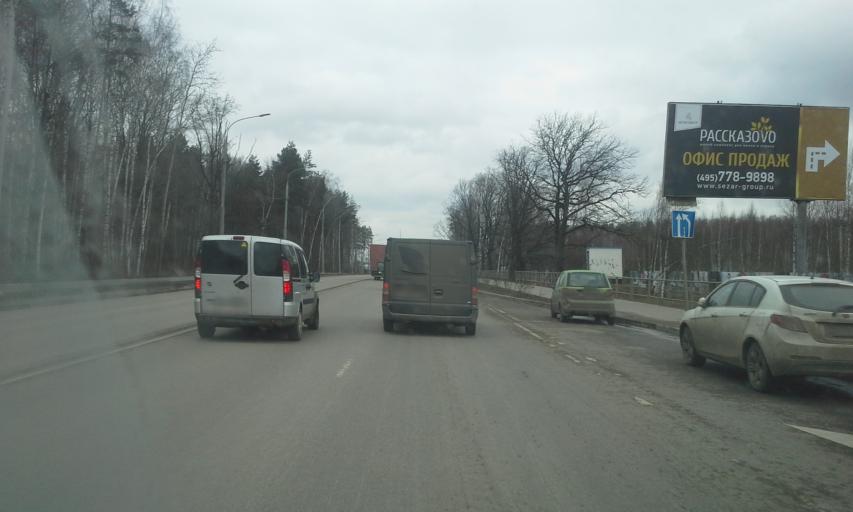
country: RU
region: Moscow
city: Novo-Peredelkino
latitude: 55.6229
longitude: 37.3381
